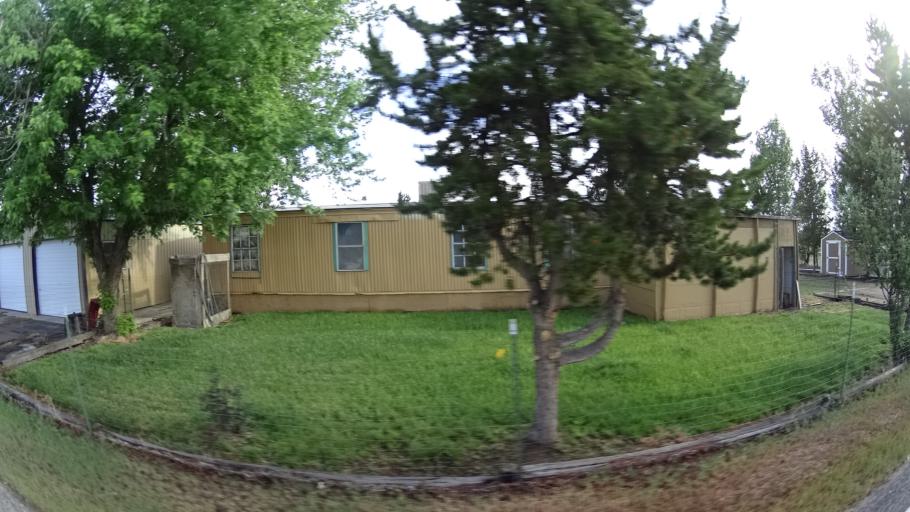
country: US
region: Idaho
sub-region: Ada County
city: Star
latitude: 43.7718
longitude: -116.4911
